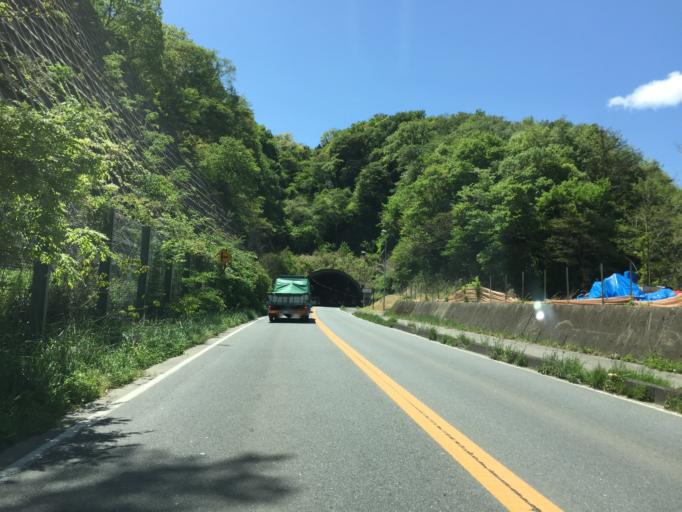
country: JP
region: Fukushima
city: Iwaki
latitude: 36.9606
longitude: 140.8713
